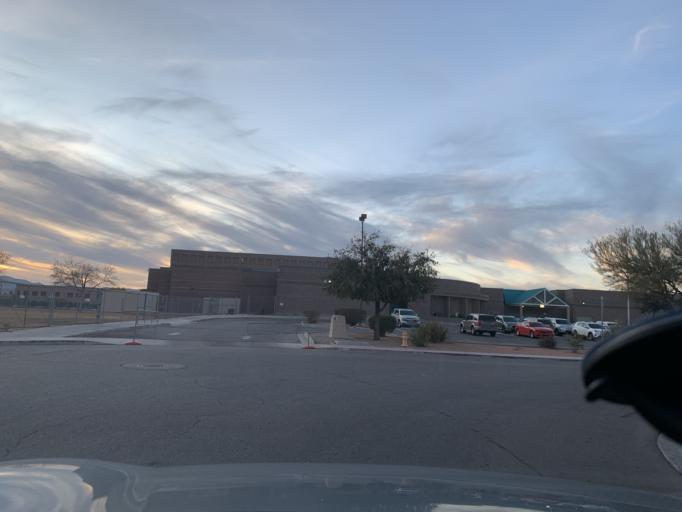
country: US
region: Nevada
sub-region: Clark County
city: Spring Valley
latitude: 36.0889
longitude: -115.2360
